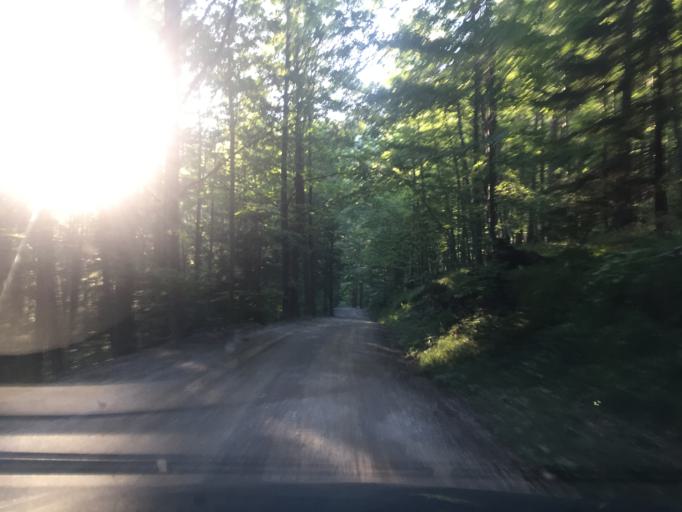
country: SI
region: Ravne na Koroskem
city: Kotlje
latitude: 46.4734
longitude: 14.9795
